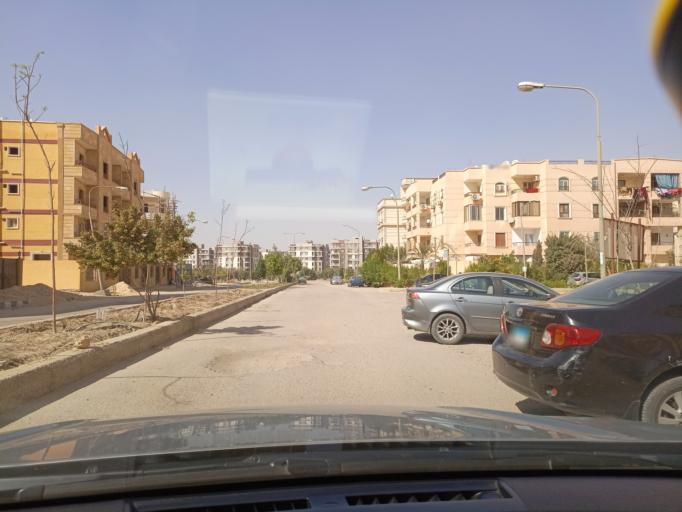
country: EG
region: Muhafazat al Qalyubiyah
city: Al Khankah
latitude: 30.2267
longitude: 31.4449
